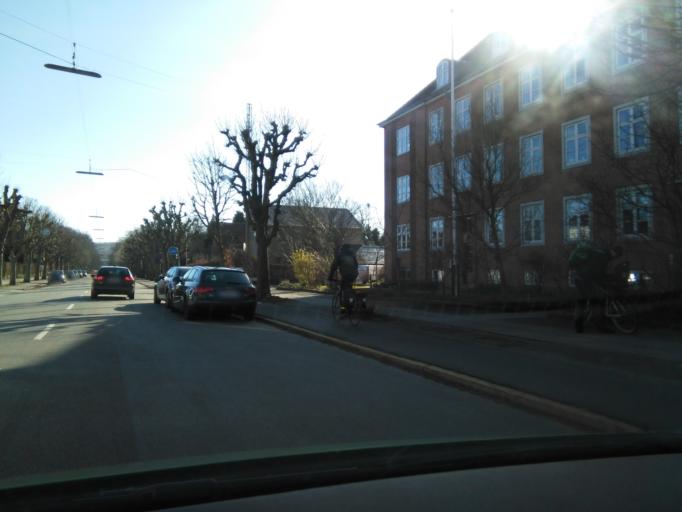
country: DK
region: Central Jutland
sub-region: Arhus Kommune
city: Arhus
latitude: 56.1397
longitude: 10.1948
